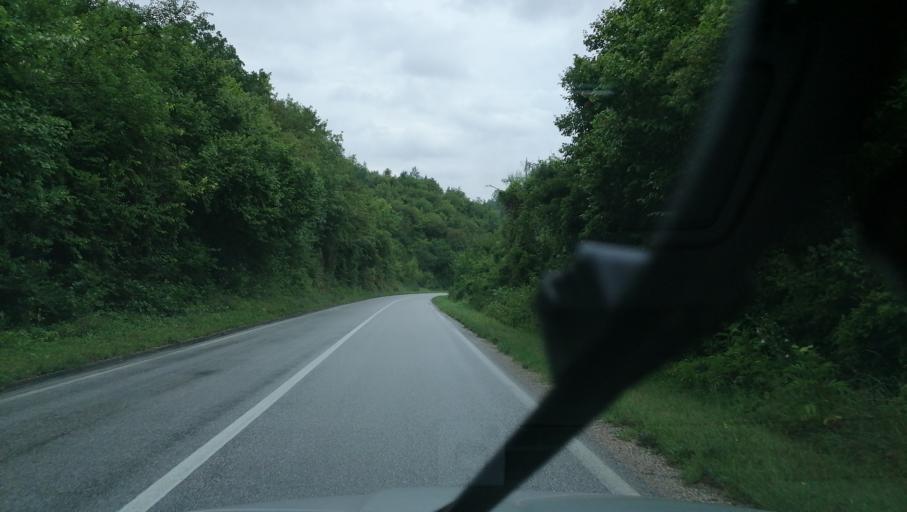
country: RS
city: Durici
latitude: 43.7542
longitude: 19.3986
